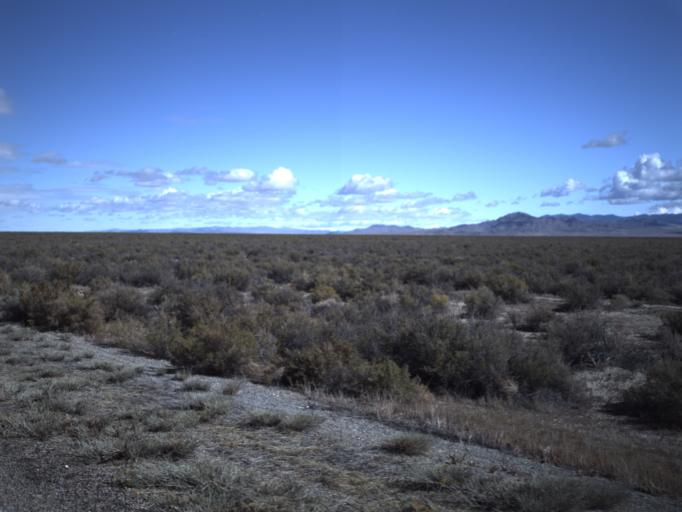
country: US
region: Nevada
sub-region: White Pine County
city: McGill
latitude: 39.0261
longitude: -114.0356
